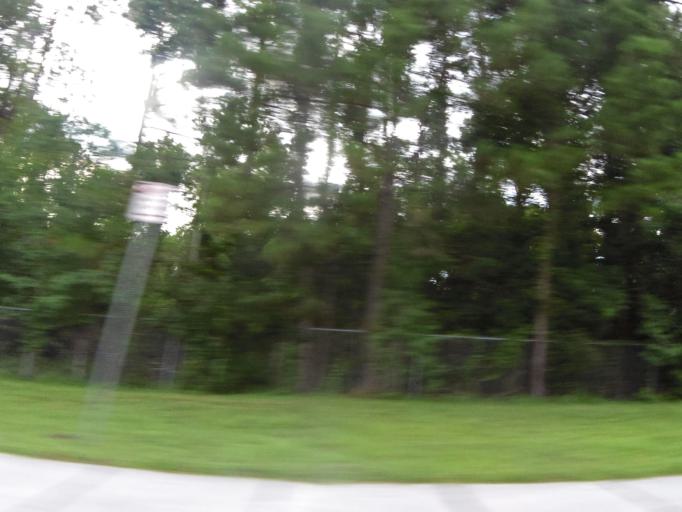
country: US
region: Florida
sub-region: Clay County
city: Bellair-Meadowbrook Terrace
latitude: 30.3021
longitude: -81.8238
